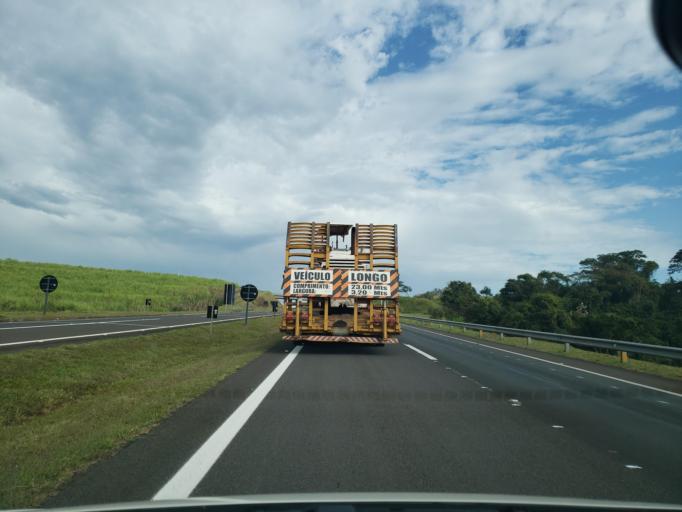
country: BR
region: Sao Paulo
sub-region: Dois Corregos
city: Dois Corregos
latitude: -22.2492
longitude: -48.3559
